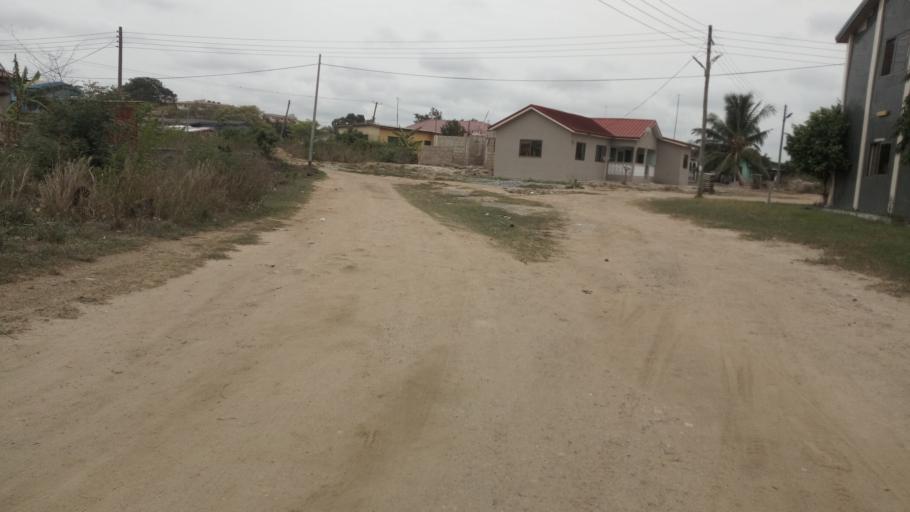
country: GH
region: Central
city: Winneba
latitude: 5.3647
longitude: -0.6397
